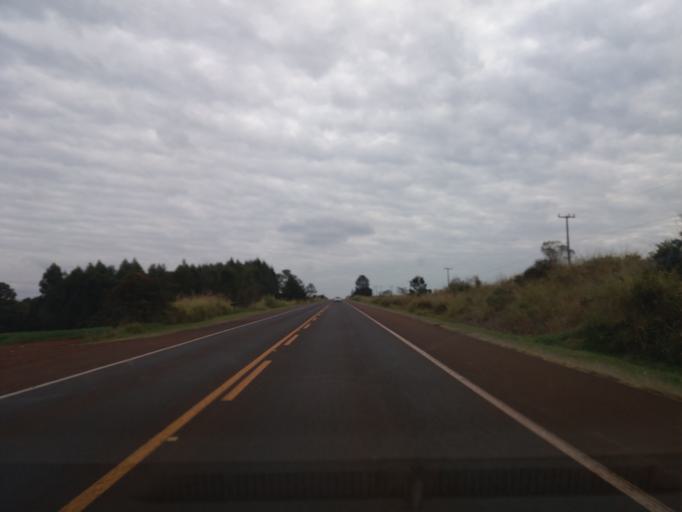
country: BR
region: Parana
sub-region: Corbelia
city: Corbelia
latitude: -24.8976
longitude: -53.3575
